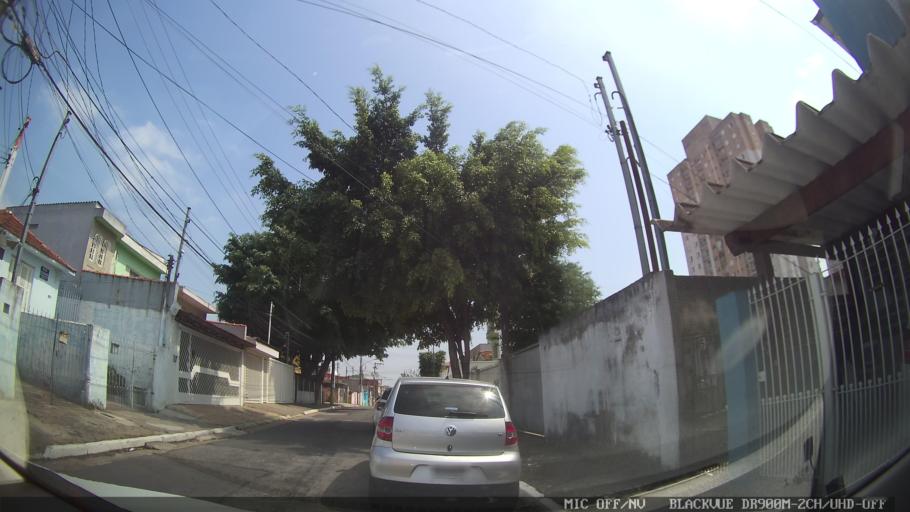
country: BR
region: Sao Paulo
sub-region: Sao Paulo
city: Sao Paulo
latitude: -23.5084
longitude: -46.6720
